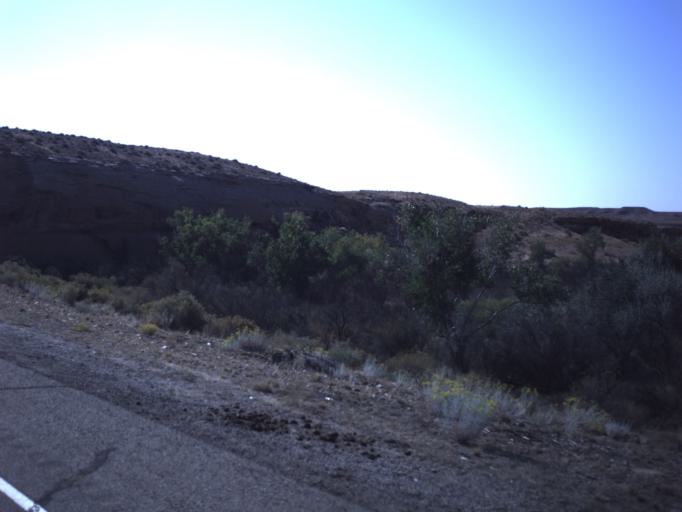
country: US
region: Utah
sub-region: San Juan County
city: Blanding
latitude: 37.2564
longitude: -109.6173
